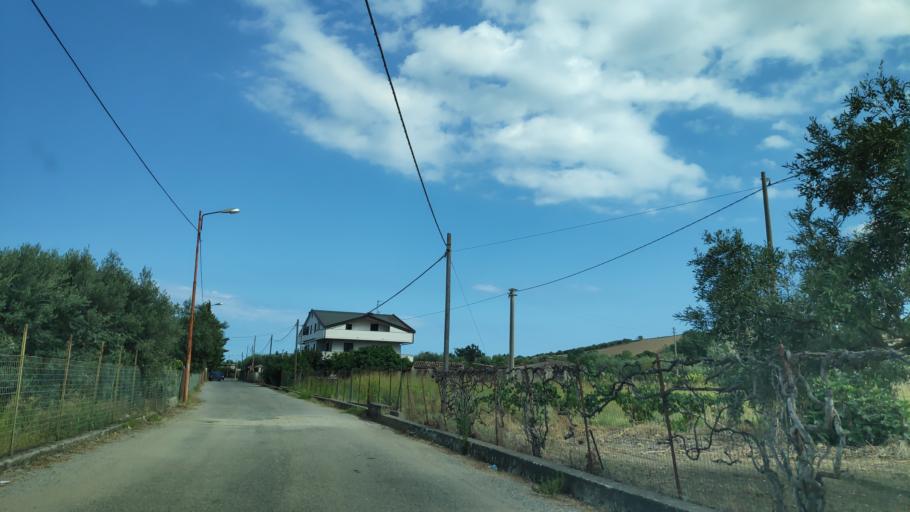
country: IT
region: Calabria
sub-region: Provincia di Catanzaro
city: Guardavalle Marina
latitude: 38.4640
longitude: 16.5735
